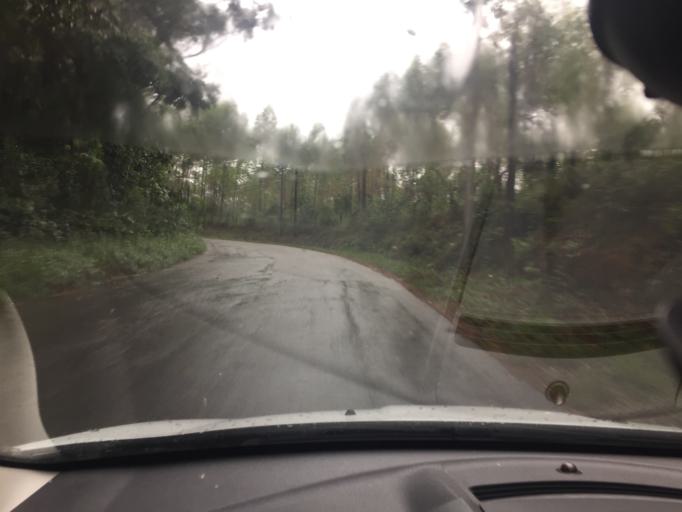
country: BR
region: Sao Paulo
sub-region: Varzea Paulista
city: Varzea Paulista
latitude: -23.2632
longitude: -46.8800
